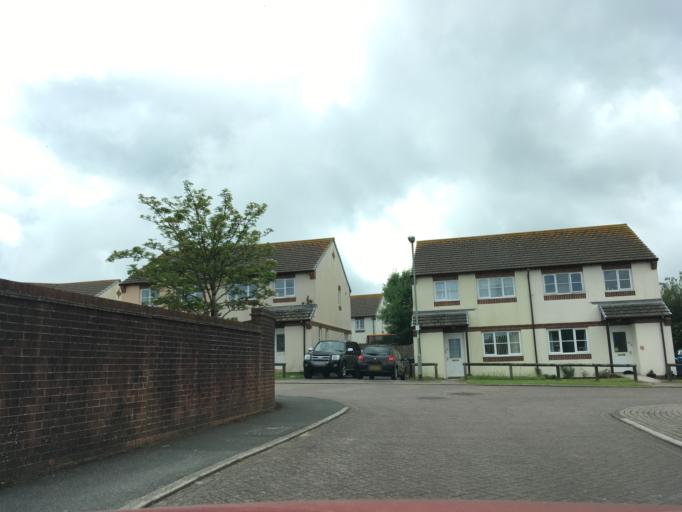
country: GB
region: England
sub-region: Devon
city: Dartmouth
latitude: 50.3487
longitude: -3.6001
